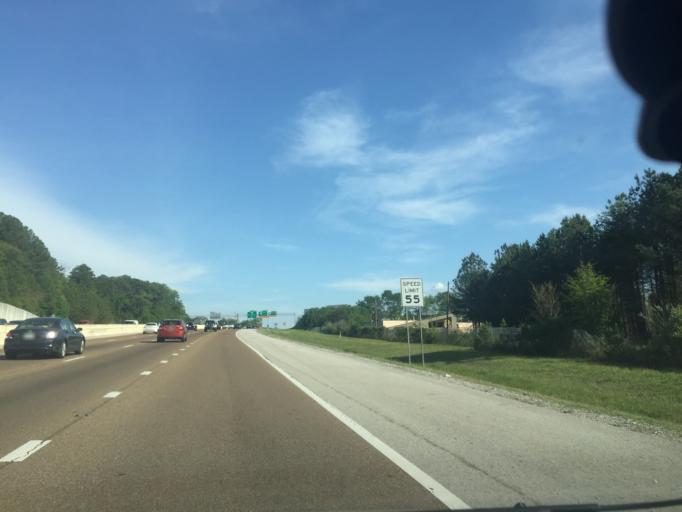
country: US
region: Tennessee
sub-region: Hamilton County
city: East Chattanooga
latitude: 35.0855
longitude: -85.2109
